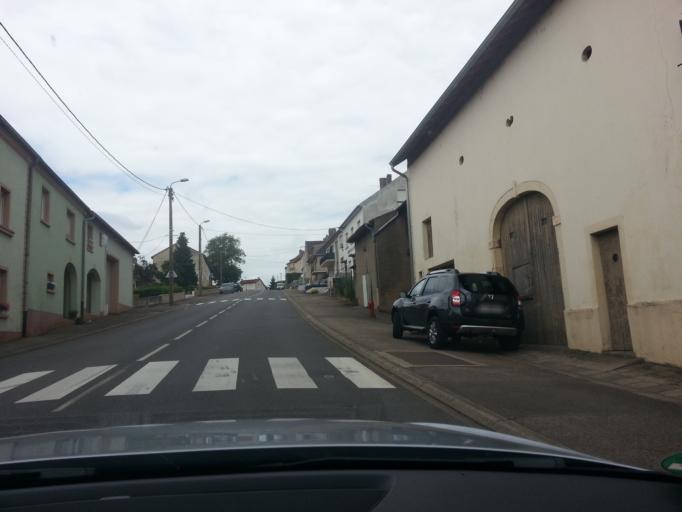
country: DE
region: Saarland
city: Perl
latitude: 49.4606
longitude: 6.3741
